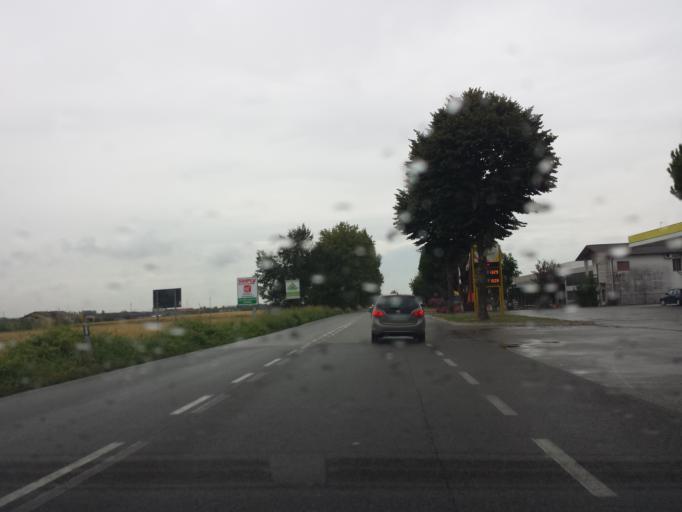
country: IT
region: Veneto
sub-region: Provincia di Verona
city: Locara
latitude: 45.4320
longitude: 11.3542
